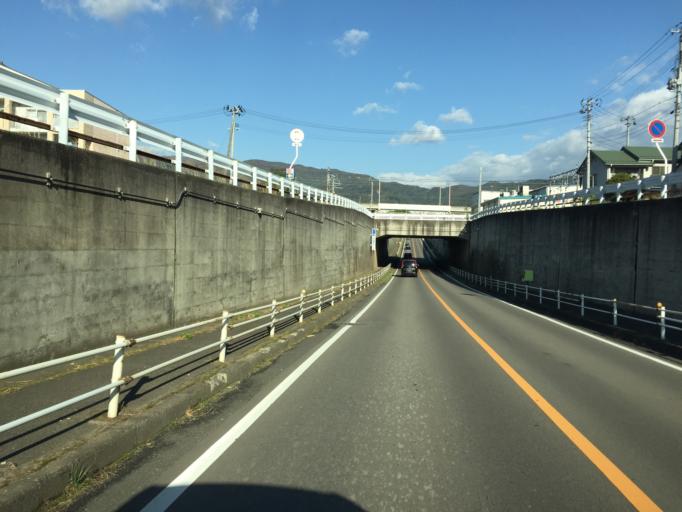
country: JP
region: Fukushima
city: Hobaramachi
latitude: 37.8764
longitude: 140.5374
